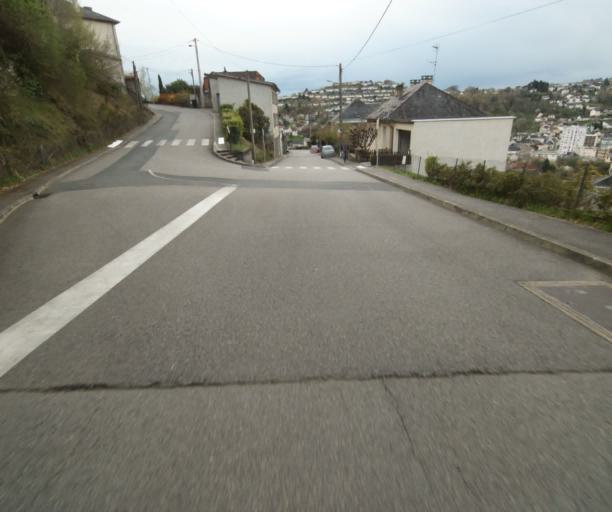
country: FR
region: Limousin
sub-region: Departement de la Correze
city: Tulle
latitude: 45.2604
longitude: 1.7604
